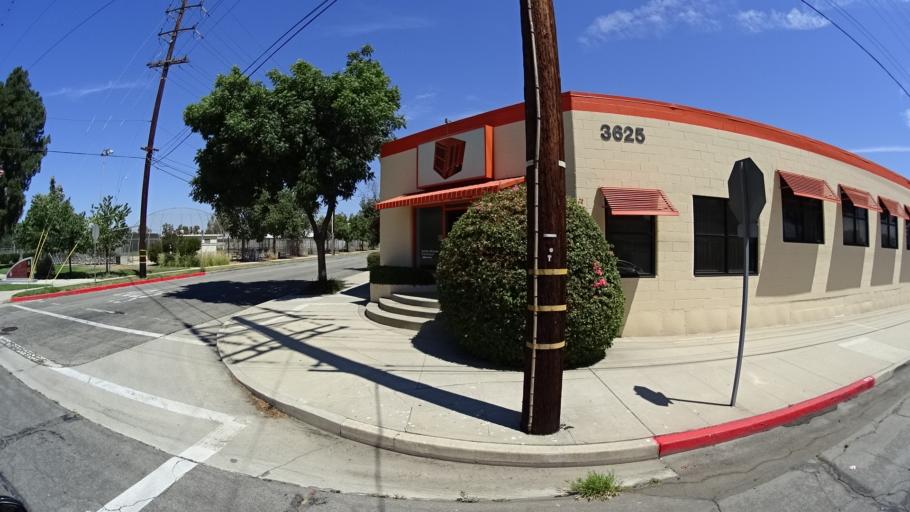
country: US
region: California
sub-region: Los Angeles County
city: North Hollywood
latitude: 34.1884
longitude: -118.3511
